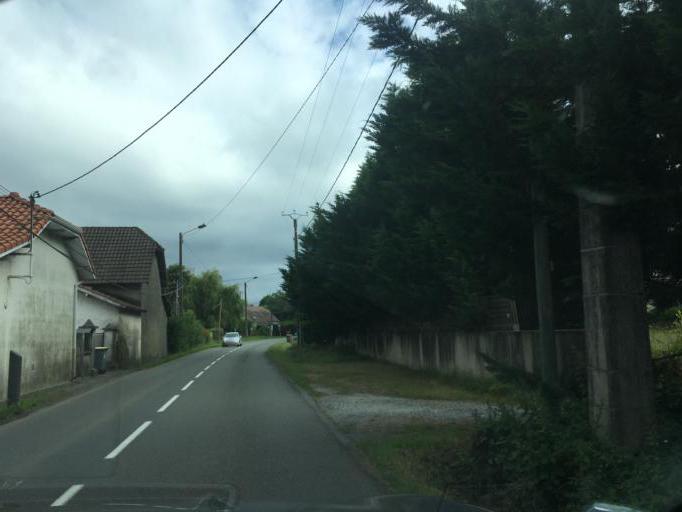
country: FR
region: Aquitaine
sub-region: Departement des Pyrenees-Atlantiques
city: Ousse
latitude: 43.3004
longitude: -0.2734
